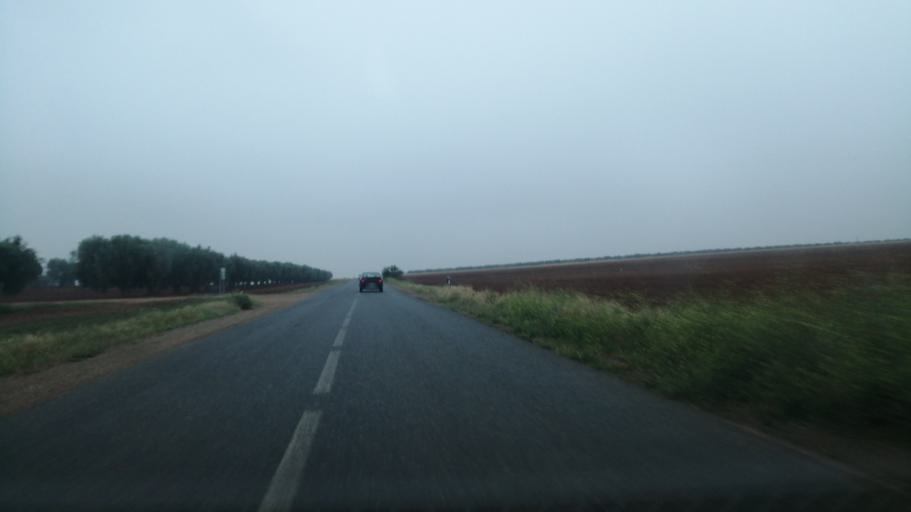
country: MA
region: Rabat-Sale-Zemmour-Zaer
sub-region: Khemisset
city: Tiflet
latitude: 33.7495
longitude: -6.2676
